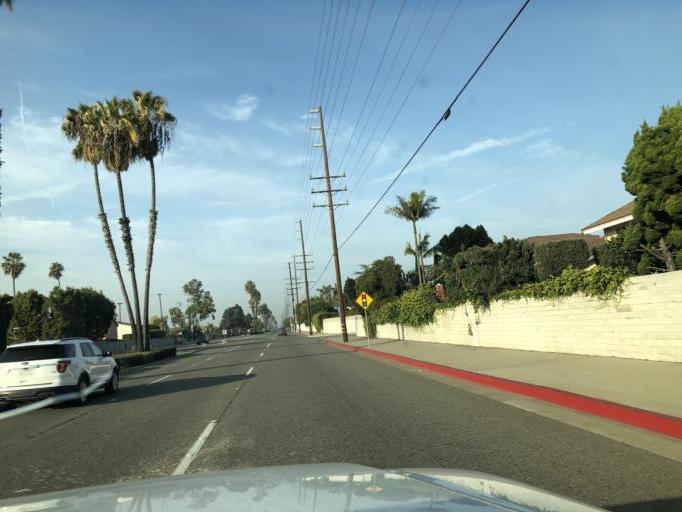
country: US
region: California
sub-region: Orange County
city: Costa Mesa
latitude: 33.6634
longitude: -117.9537
